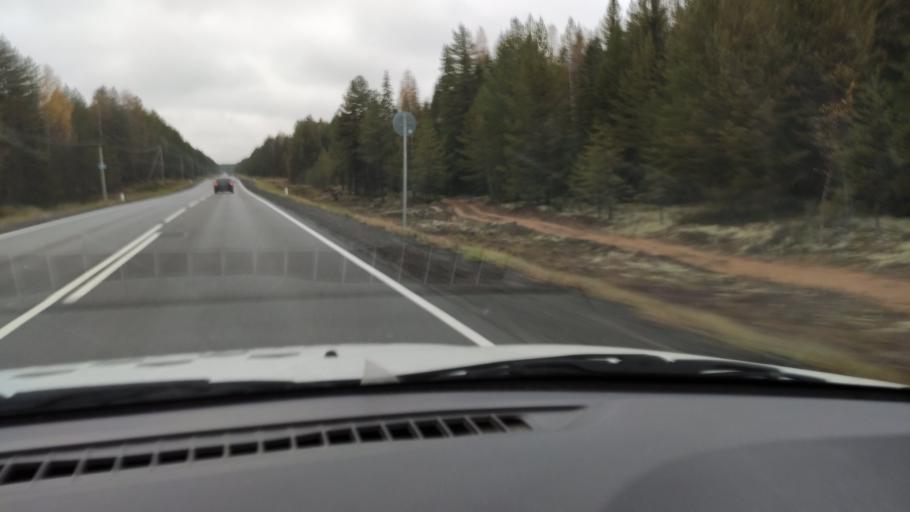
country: RU
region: Kirov
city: Belaya Kholunitsa
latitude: 58.9066
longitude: 51.0170
